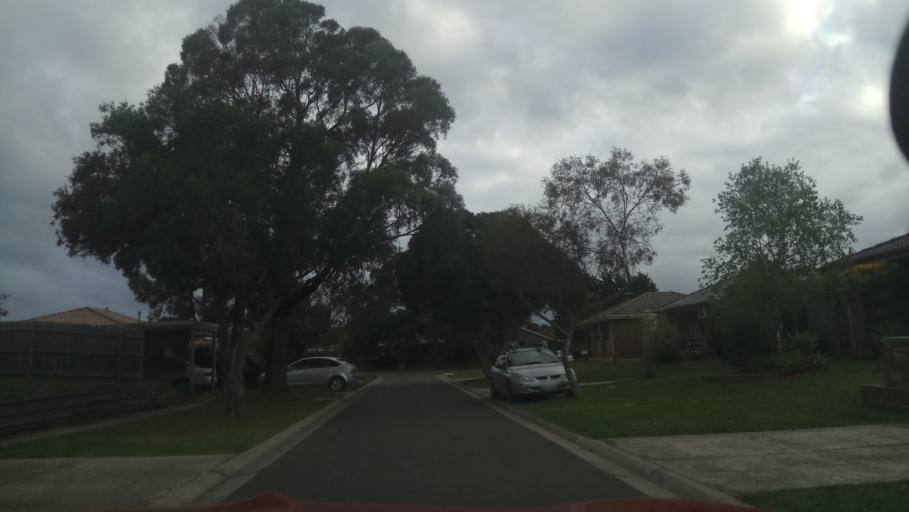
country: AU
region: Victoria
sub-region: Casey
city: Cranbourne North
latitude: -38.0733
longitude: 145.2649
